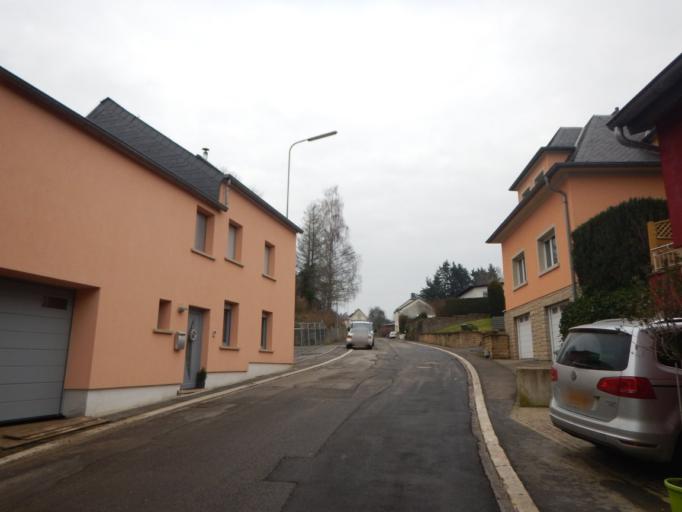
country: LU
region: Luxembourg
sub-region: Canton de Capellen
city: Koerich
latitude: 49.6702
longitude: 5.9501
